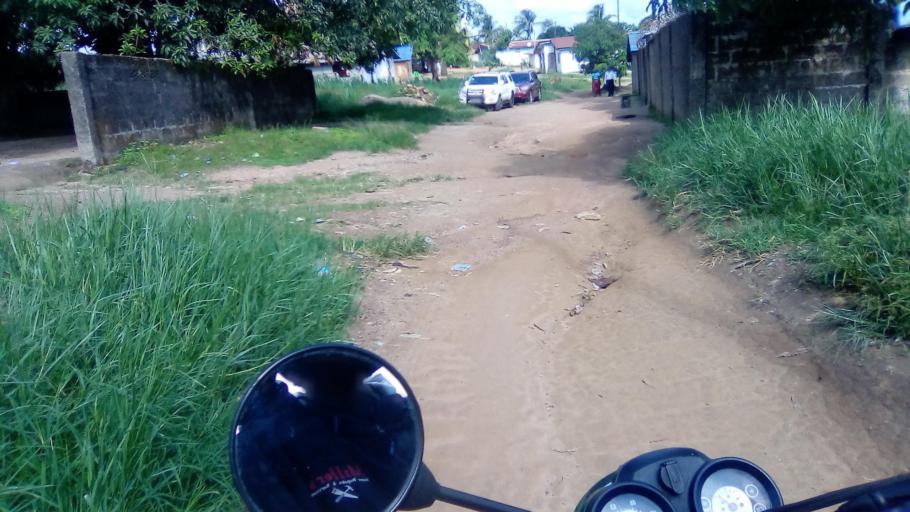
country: SL
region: Southern Province
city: Bo
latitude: 7.9588
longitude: -11.7534
